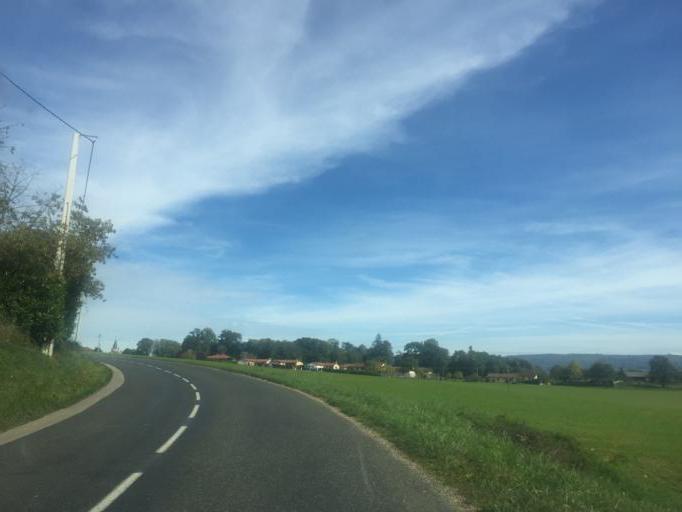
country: FR
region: Franche-Comte
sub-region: Departement du Jura
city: Saint-Amour
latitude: 46.4165
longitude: 5.2888
